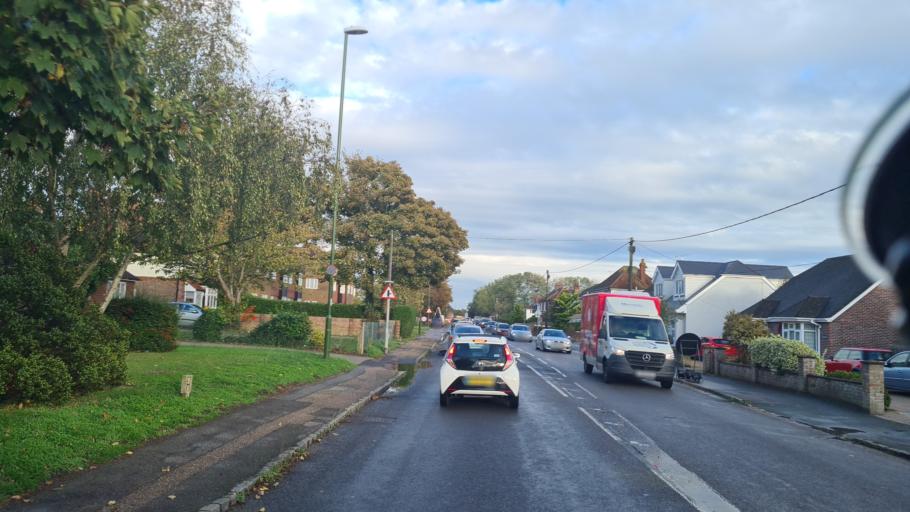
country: GB
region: England
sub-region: West Sussex
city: Littlehampton
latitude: 50.8213
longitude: -0.5426
